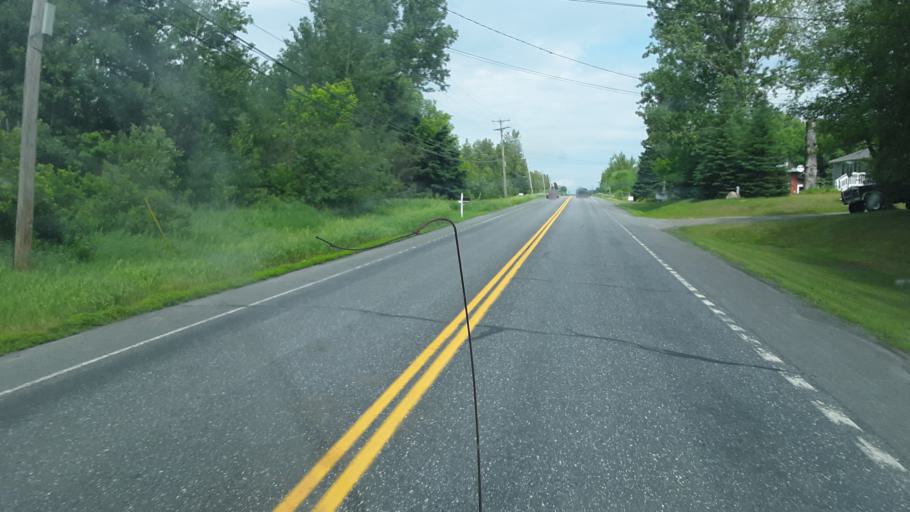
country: US
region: Maine
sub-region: Aroostook County
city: Fort Fairfield
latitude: 46.7616
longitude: -67.8560
